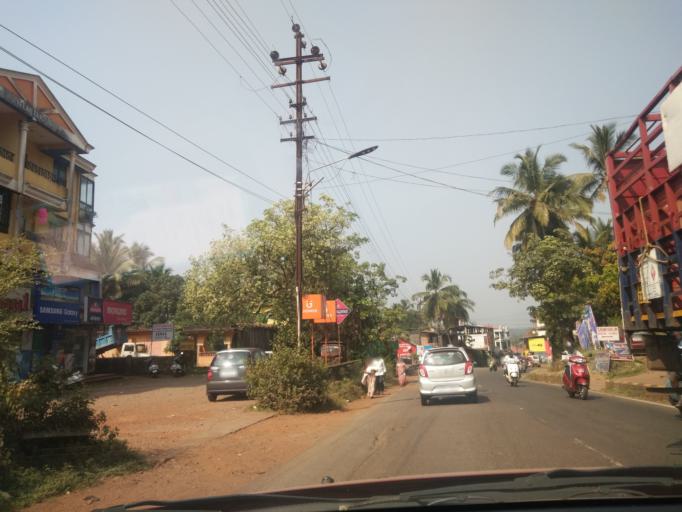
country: IN
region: Goa
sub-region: North Goa
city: Sanquelim
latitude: 15.5579
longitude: 74.0151
